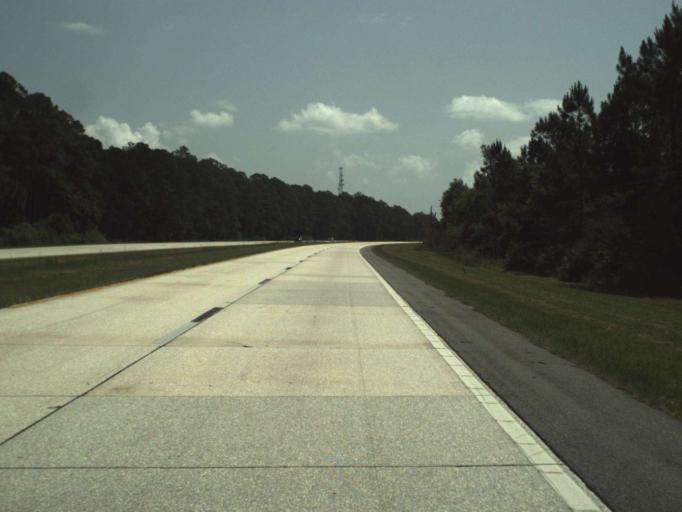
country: US
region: Florida
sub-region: Volusia County
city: Samsula-Spruce Creek
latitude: 29.1312
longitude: -81.1554
